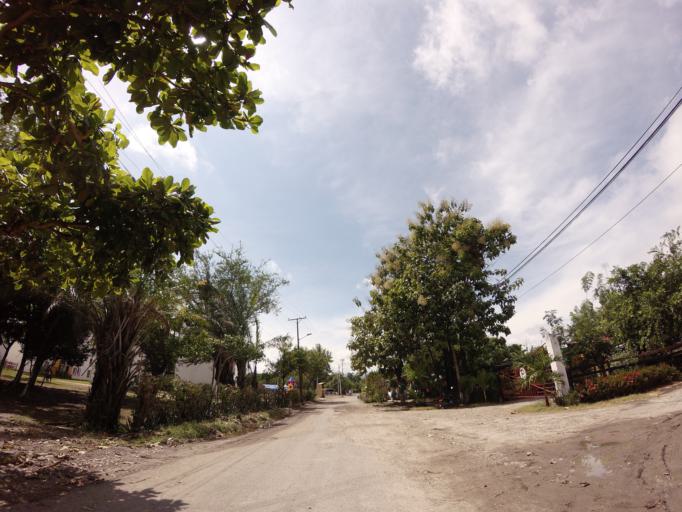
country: CO
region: Cundinamarca
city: Puerto Salgar
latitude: 5.4794
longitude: -74.6774
